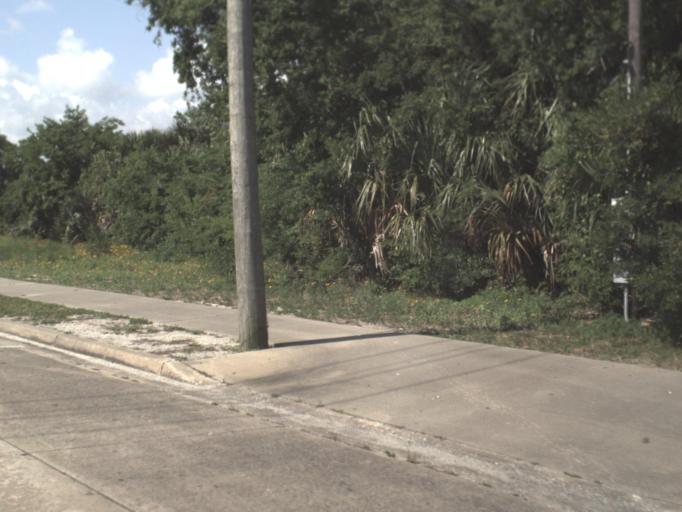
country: US
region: Florida
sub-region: Saint Johns County
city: Saint Augustine
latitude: 29.9068
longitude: -81.3215
